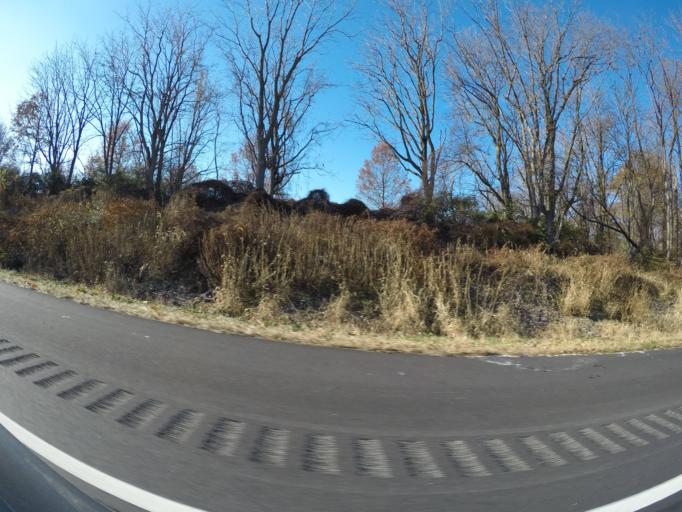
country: US
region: Pennsylvania
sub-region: Chester County
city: Oxford
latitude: 39.7619
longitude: -76.0184
